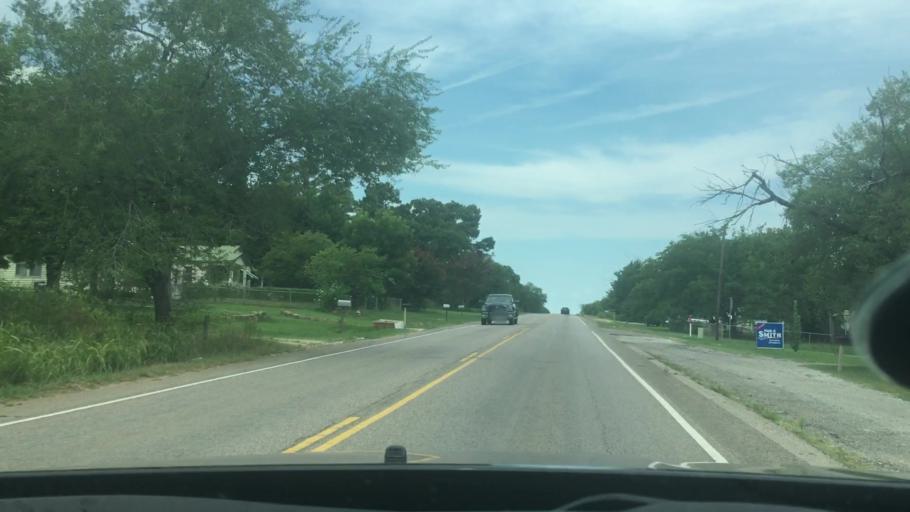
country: US
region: Oklahoma
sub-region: Seminole County
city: Seminole
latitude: 35.2359
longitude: -96.6908
